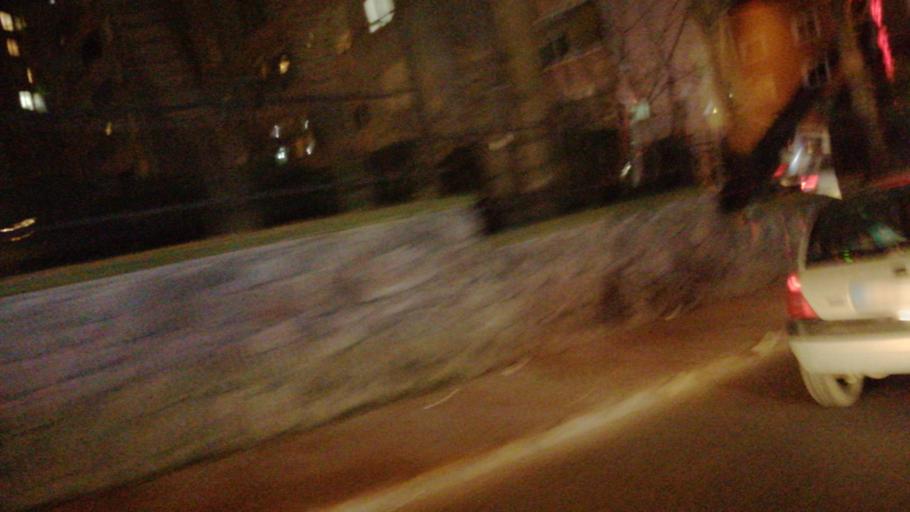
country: TR
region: Istanbul
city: Umraniye
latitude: 41.0187
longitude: 29.1263
